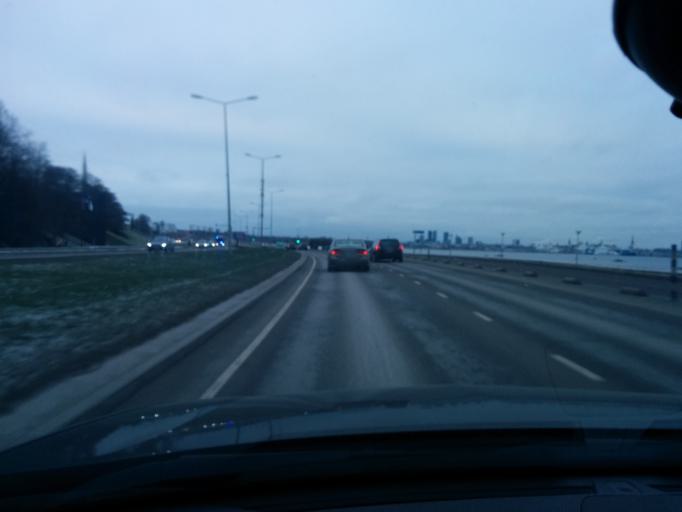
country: EE
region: Harju
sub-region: Viimsi vald
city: Viimsi
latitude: 59.4583
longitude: 24.8123
